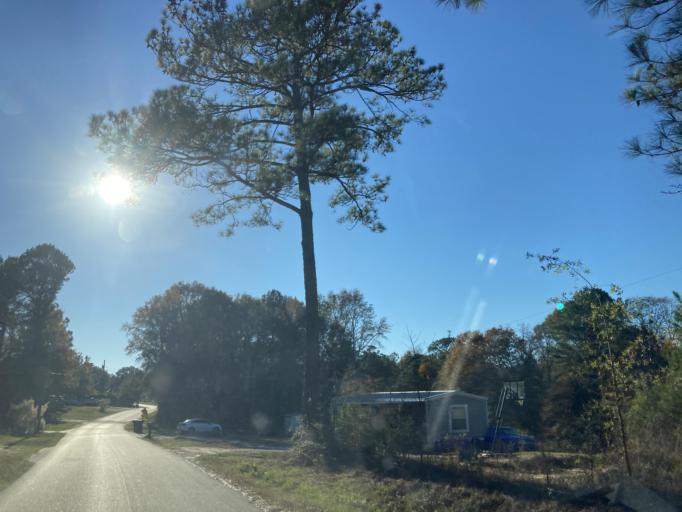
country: US
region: Mississippi
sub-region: Lamar County
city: Sumrall
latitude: 31.4010
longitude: -89.5729
